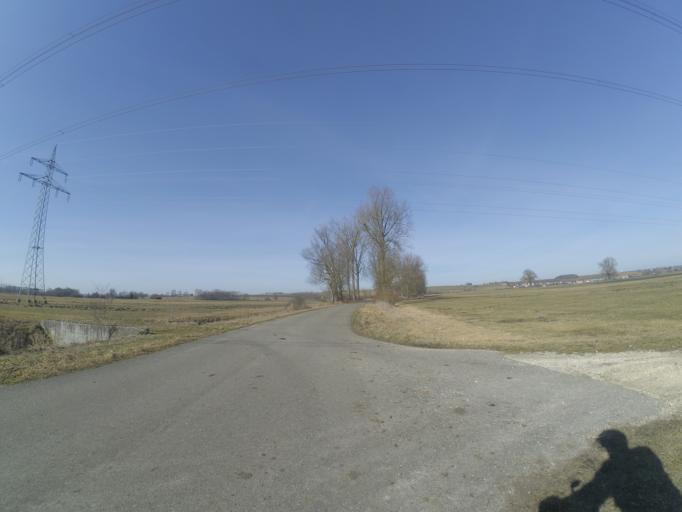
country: DE
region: Baden-Wuerttemberg
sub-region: Tuebingen Region
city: Rammingen
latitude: 48.4998
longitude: 10.1922
